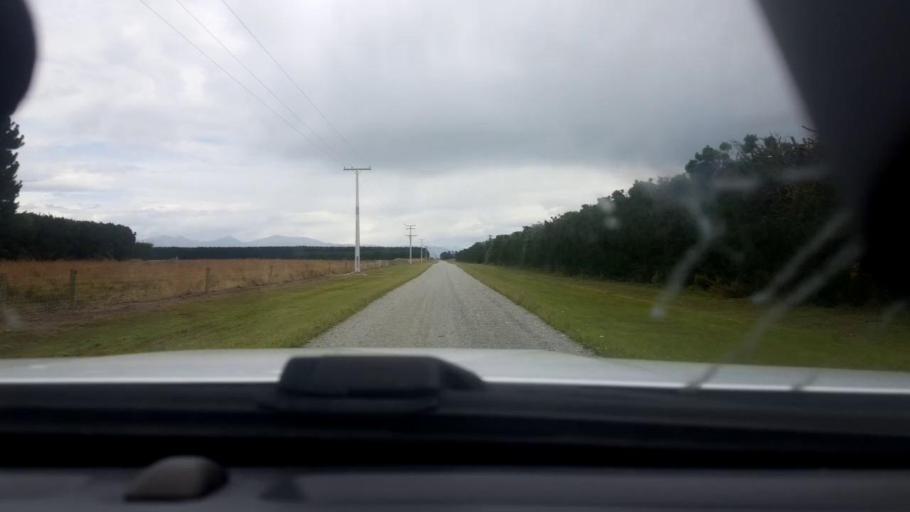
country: NZ
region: Canterbury
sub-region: Timaru District
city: Timaru
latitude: -44.1684
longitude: 171.4123
